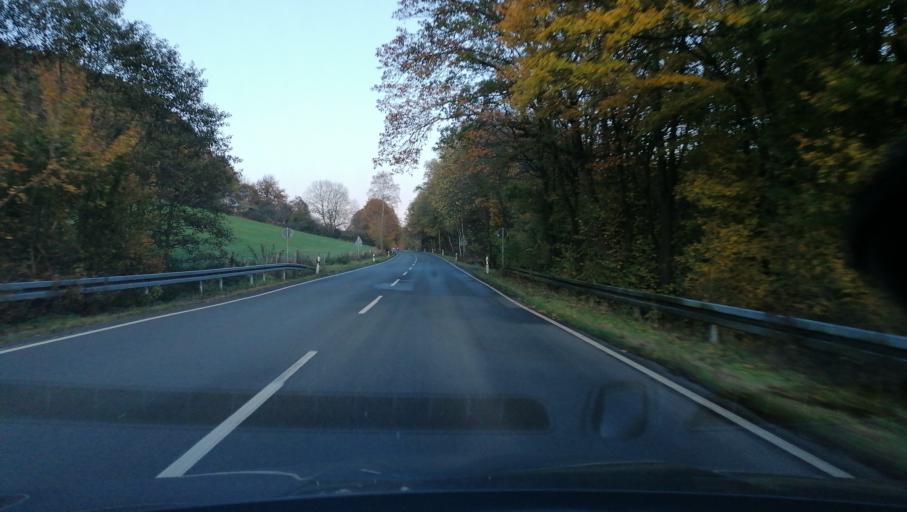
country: DE
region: North Rhine-Westphalia
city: Wetter (Ruhr)
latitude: 51.4069
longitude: 7.3875
